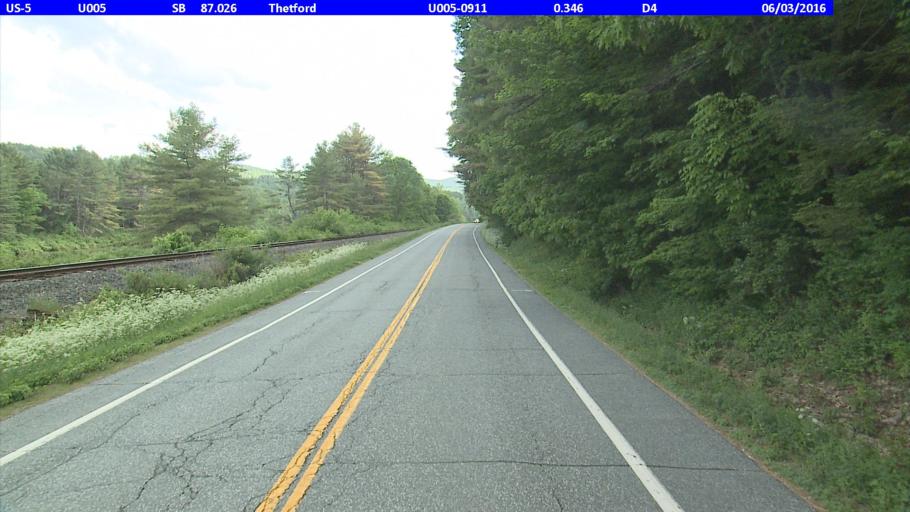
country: US
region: New Hampshire
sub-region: Grafton County
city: Lyme
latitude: 43.7767
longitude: -72.2058
